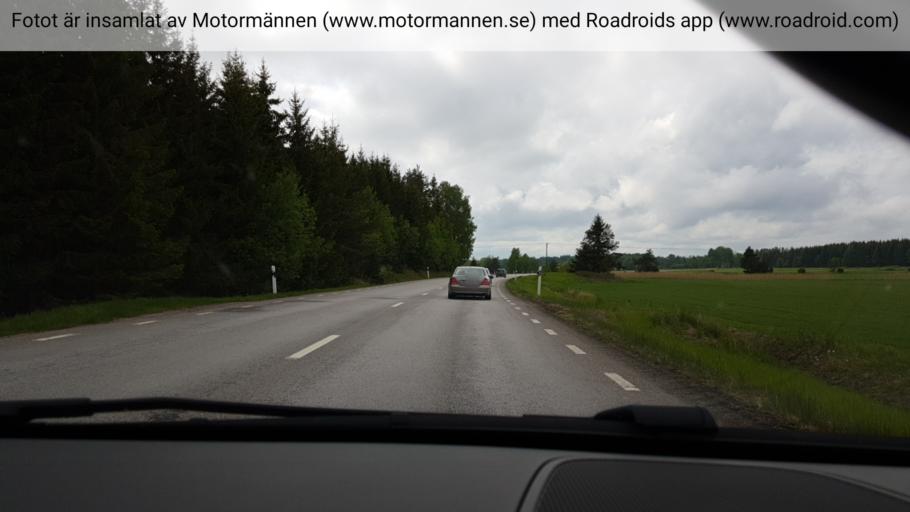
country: SE
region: Uppsala
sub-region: Osthammars Kommun
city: Osterbybruk
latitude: 60.1615
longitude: 17.9919
